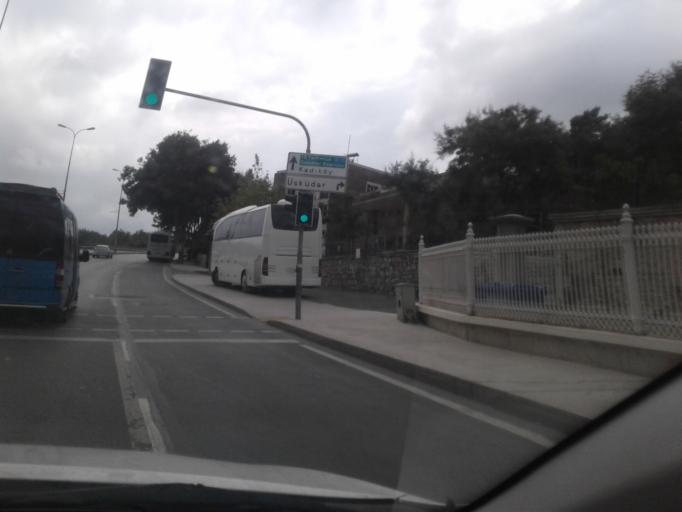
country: TR
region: Istanbul
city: UEskuedar
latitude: 41.0425
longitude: 29.0418
